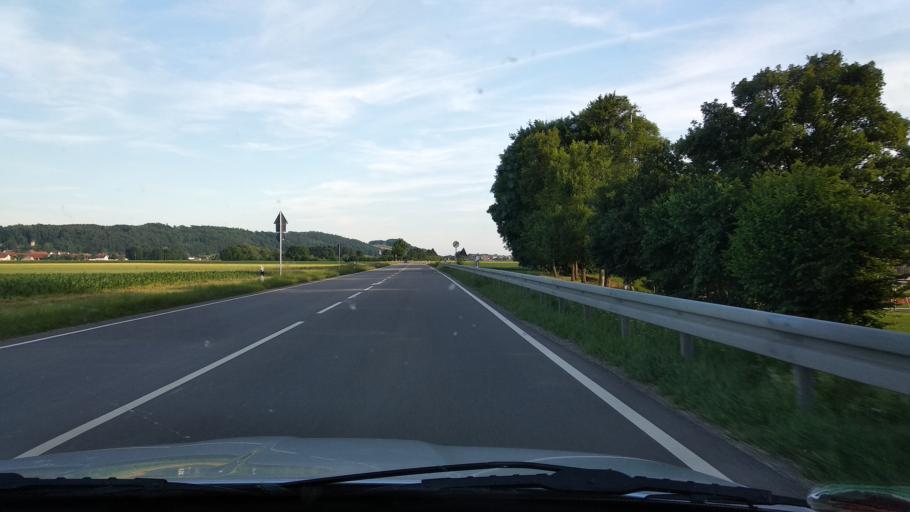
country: DE
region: Bavaria
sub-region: Swabia
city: Illertissen
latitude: 48.1977
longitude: 10.1043
